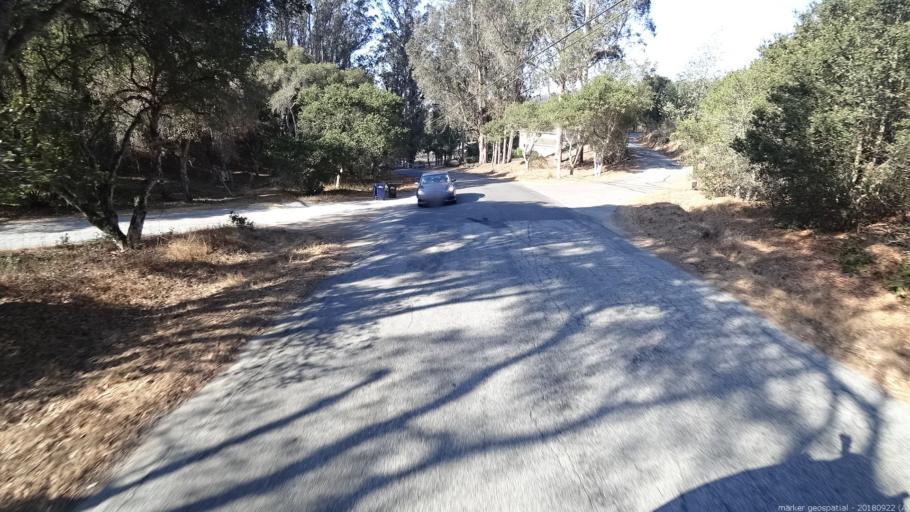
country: US
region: California
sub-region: Monterey County
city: Prunedale
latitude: 36.8244
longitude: -121.6416
